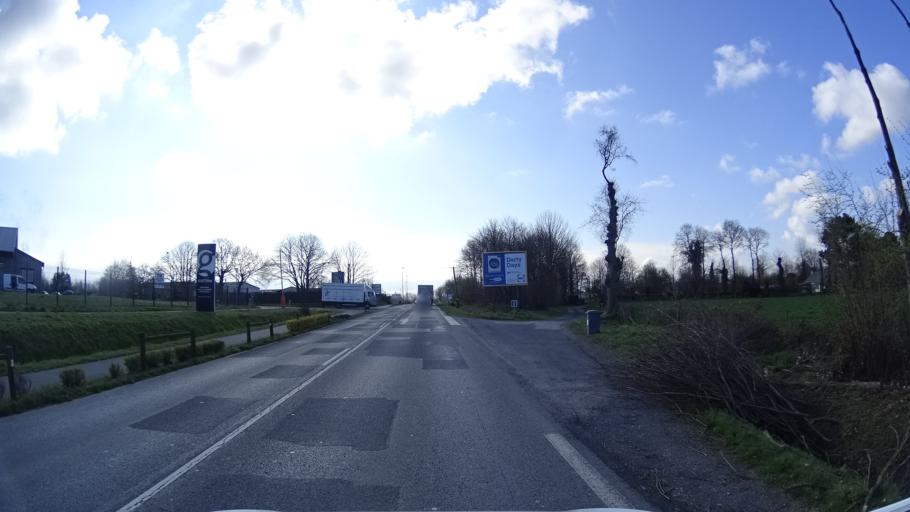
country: FR
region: Brittany
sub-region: Departement d'Ille-et-Vilaine
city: La Meziere
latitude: 48.2072
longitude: -1.7396
